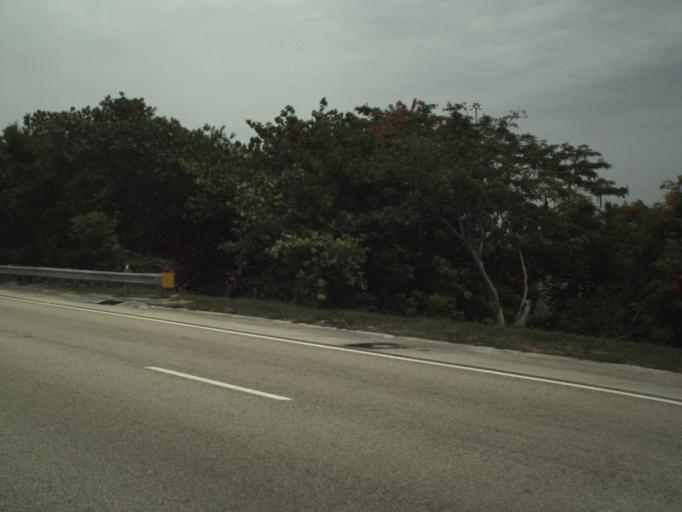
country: US
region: Florida
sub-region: Broward County
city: Dania Beach
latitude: 26.0791
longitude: -80.1340
